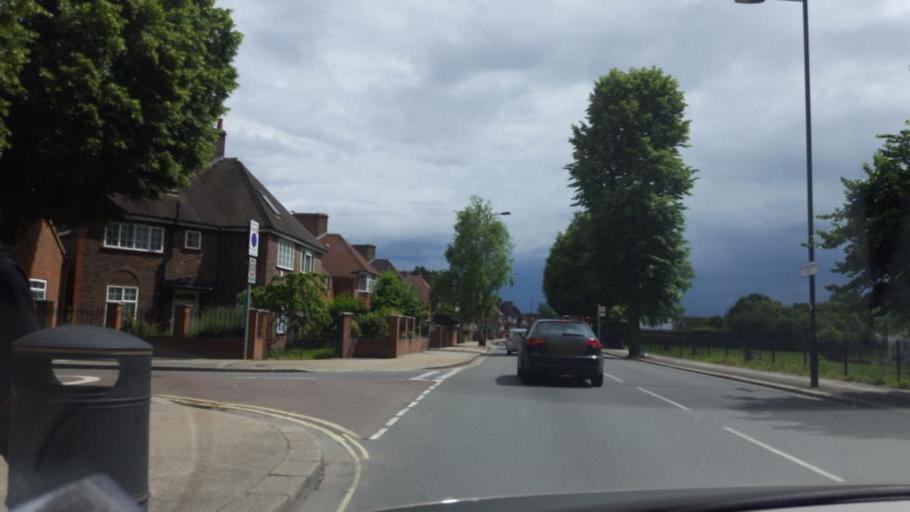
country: GB
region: England
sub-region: Greater London
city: Hammersmith
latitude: 51.5124
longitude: -0.2476
